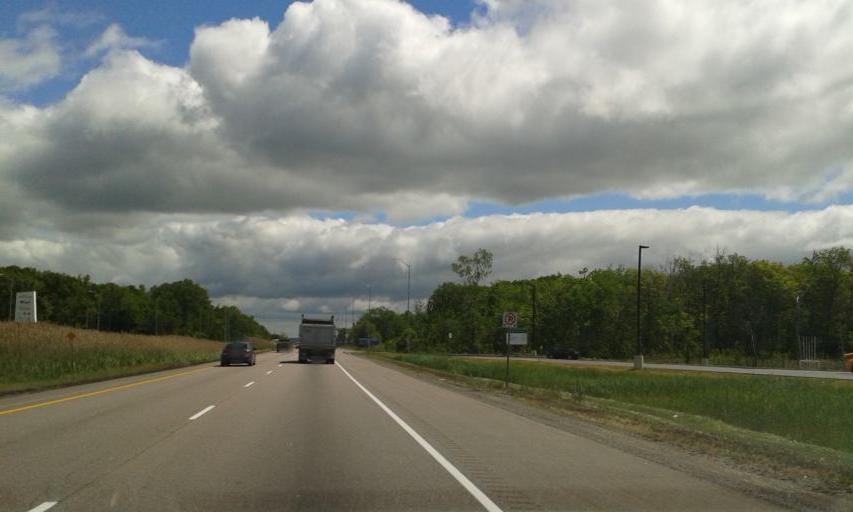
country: CA
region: Ontario
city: Quinte West
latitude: 44.1096
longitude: -77.6601
